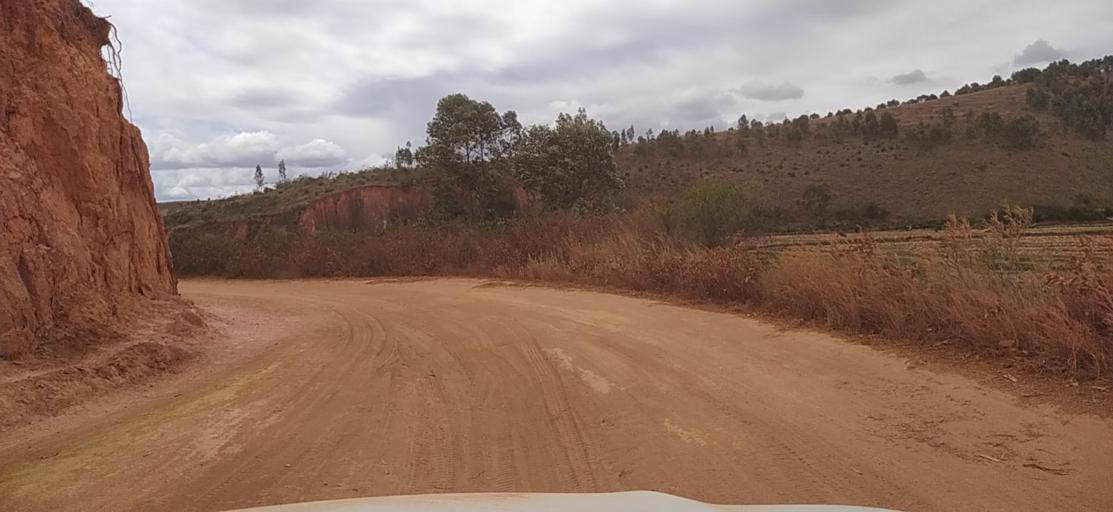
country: MG
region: Alaotra Mangoro
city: Ambatondrazaka
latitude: -18.0040
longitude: 48.2635
